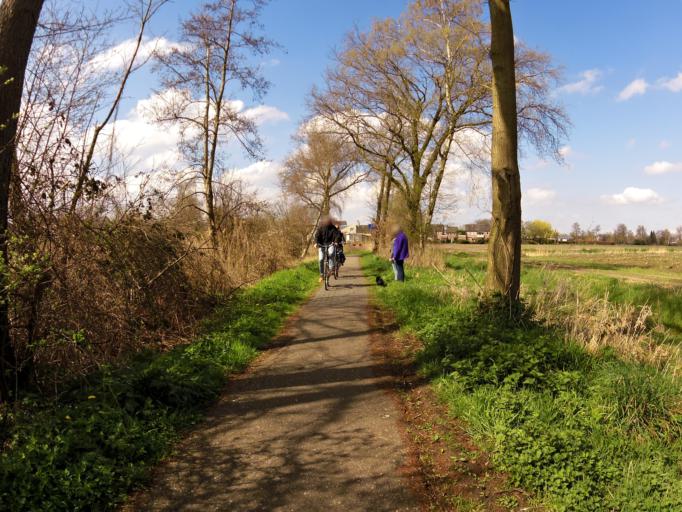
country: NL
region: North Brabant
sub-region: Gemeente Boxtel
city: Boxtel
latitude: 51.6096
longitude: 5.2963
